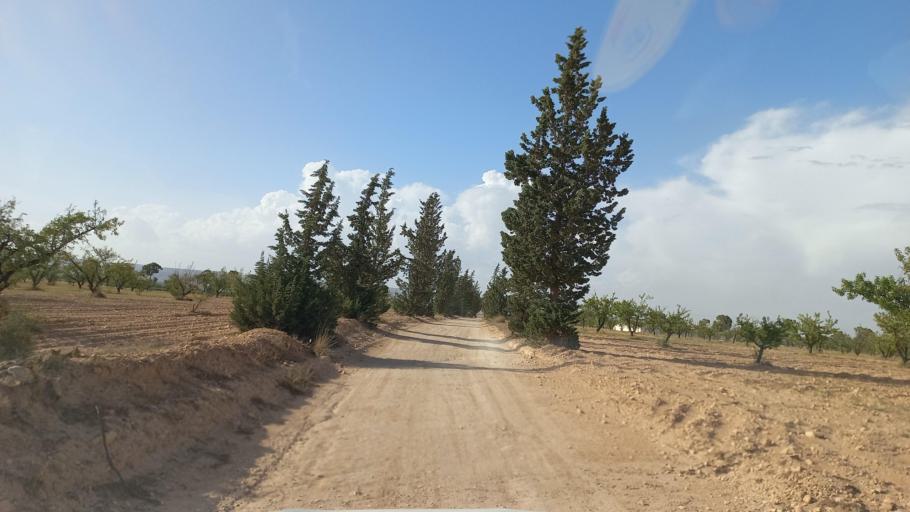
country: TN
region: Al Qasrayn
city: Kasserine
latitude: 35.2294
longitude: 8.9671
